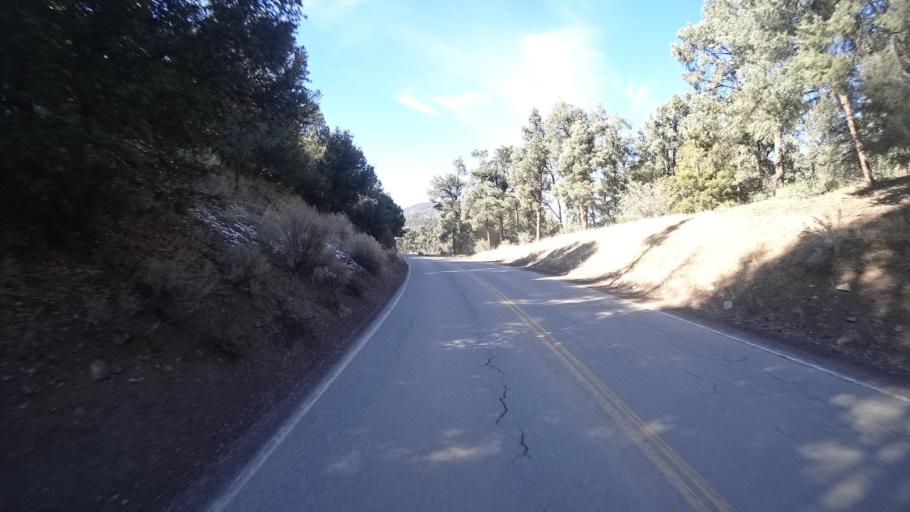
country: US
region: California
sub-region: Kern County
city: Pine Mountain Club
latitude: 34.8517
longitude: -119.1166
